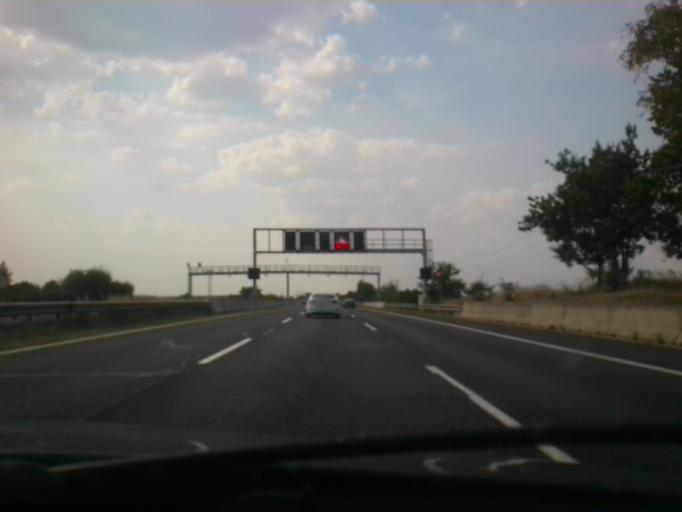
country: CZ
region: Central Bohemia
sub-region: Okres Praha-Vychod
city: Strancice
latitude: 49.9406
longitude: 14.6714
